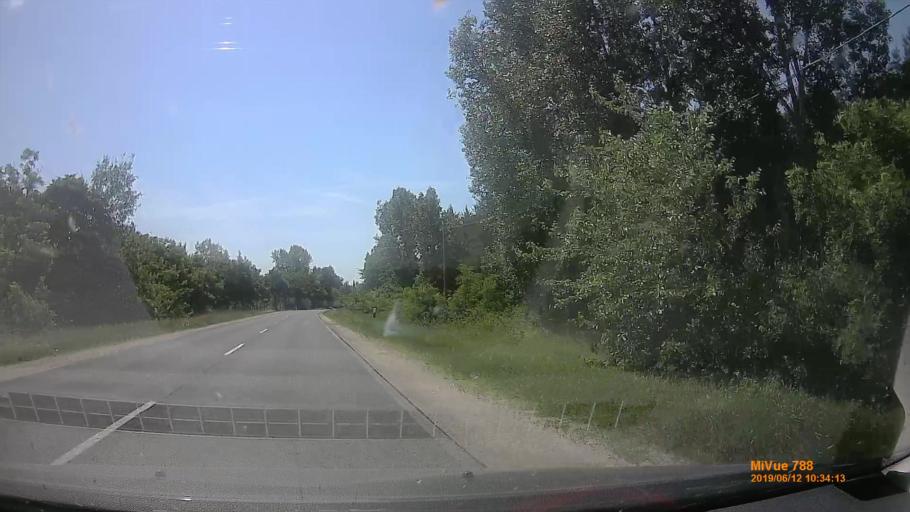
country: HU
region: Pest
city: Taborfalva
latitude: 47.0853
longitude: 19.4846
